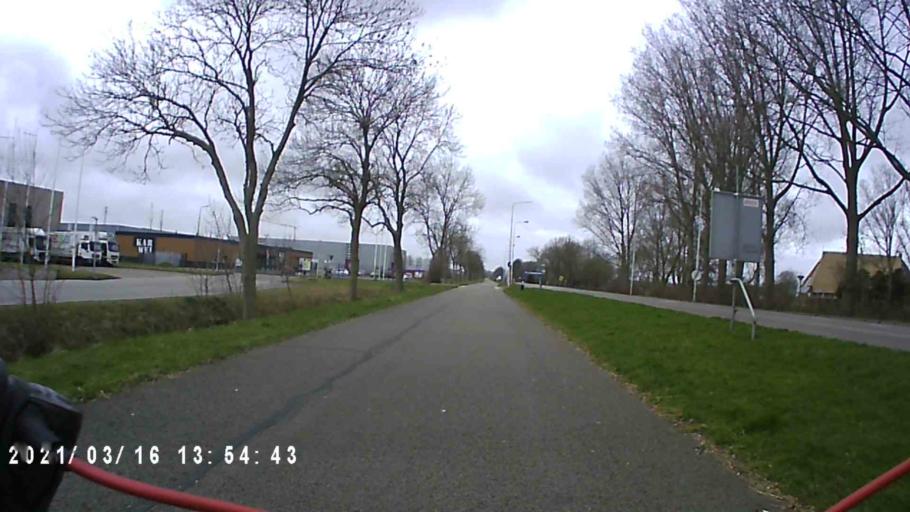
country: NL
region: Friesland
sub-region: Gemeente Franekeradeel
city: Franeker
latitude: 53.1841
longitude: 5.5208
